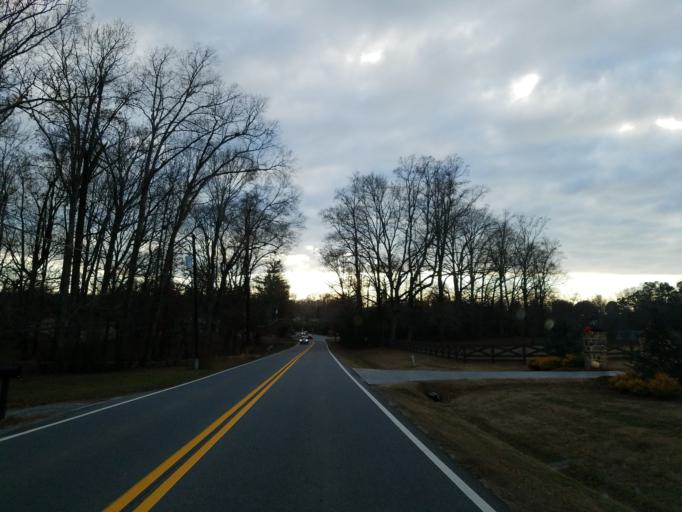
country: US
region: Georgia
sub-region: Forsyth County
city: Cumming
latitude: 34.2840
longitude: -84.0921
